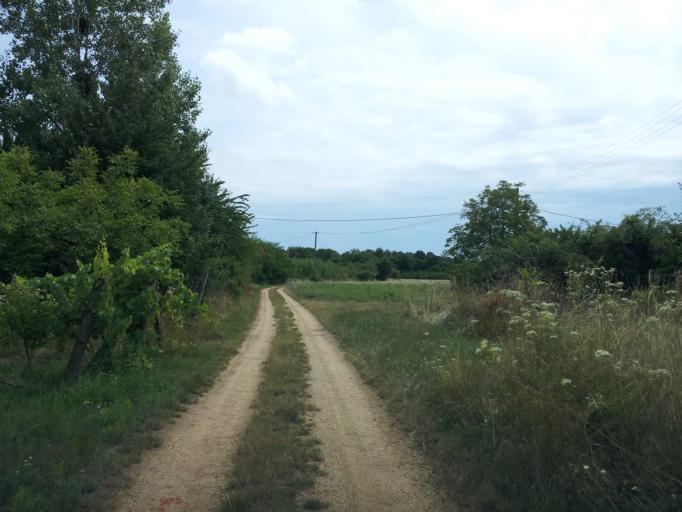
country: HU
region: Zala
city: Zalaszentgrot
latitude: 47.0084
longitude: 16.9754
